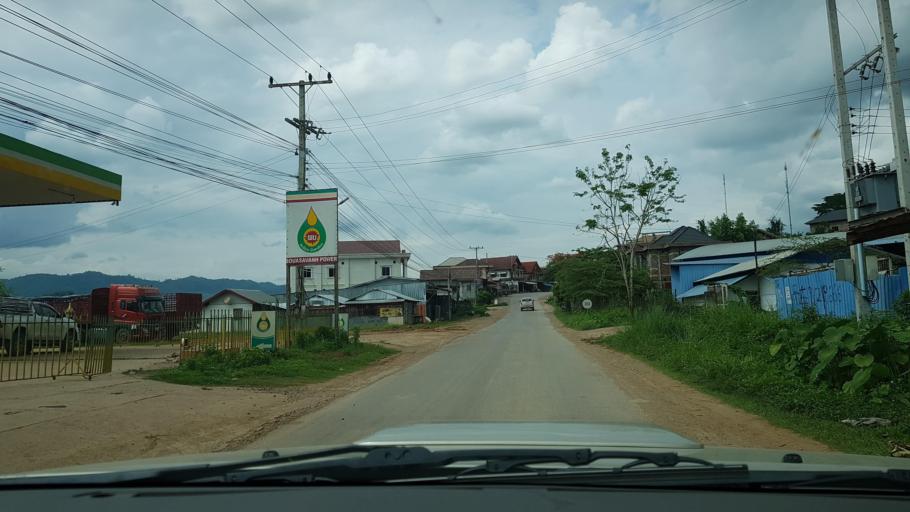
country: LA
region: Loungnamtha
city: Muang Nale
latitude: 20.2973
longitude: 101.6362
